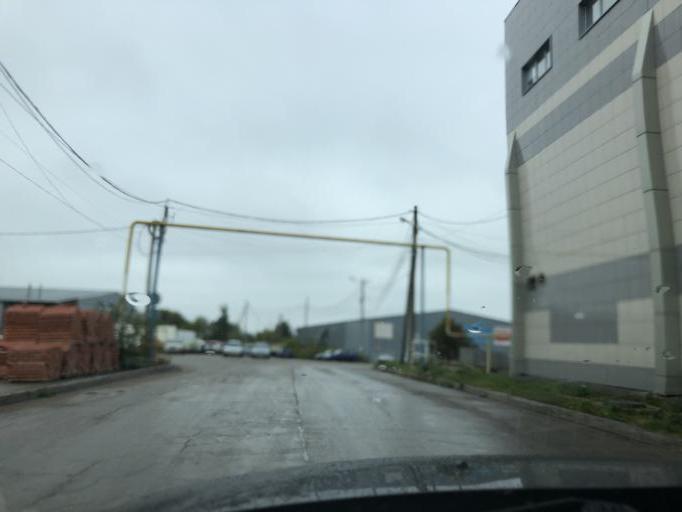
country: RU
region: Tula
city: Kosaya Gora
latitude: 54.1858
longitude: 37.5233
